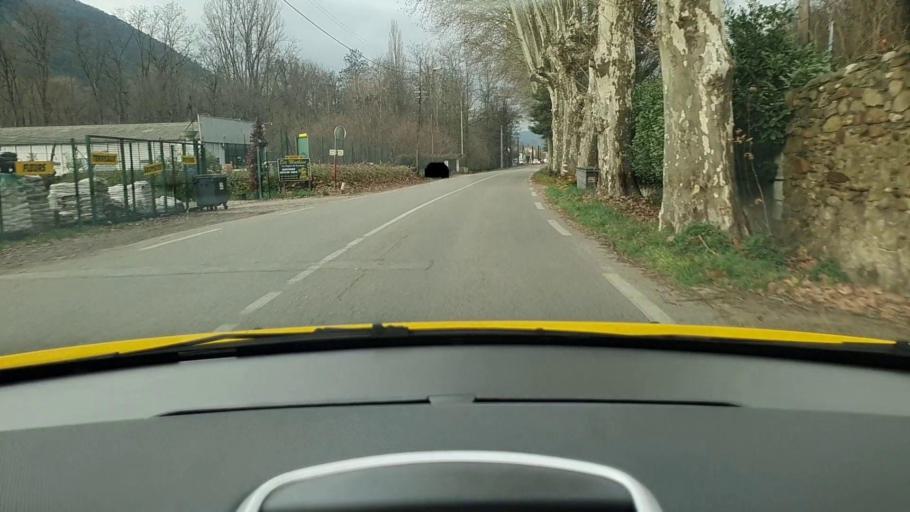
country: FR
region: Languedoc-Roussillon
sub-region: Departement du Gard
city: Besseges
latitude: 44.2851
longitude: 4.1135
